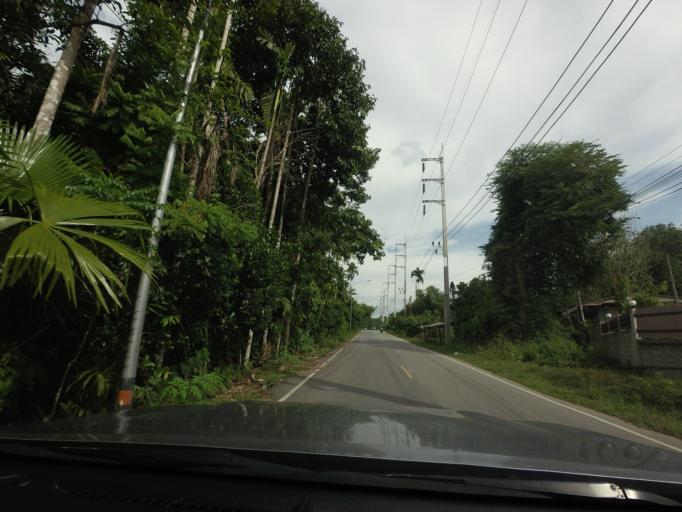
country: TH
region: Yala
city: Yala
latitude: 6.5090
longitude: 101.2882
